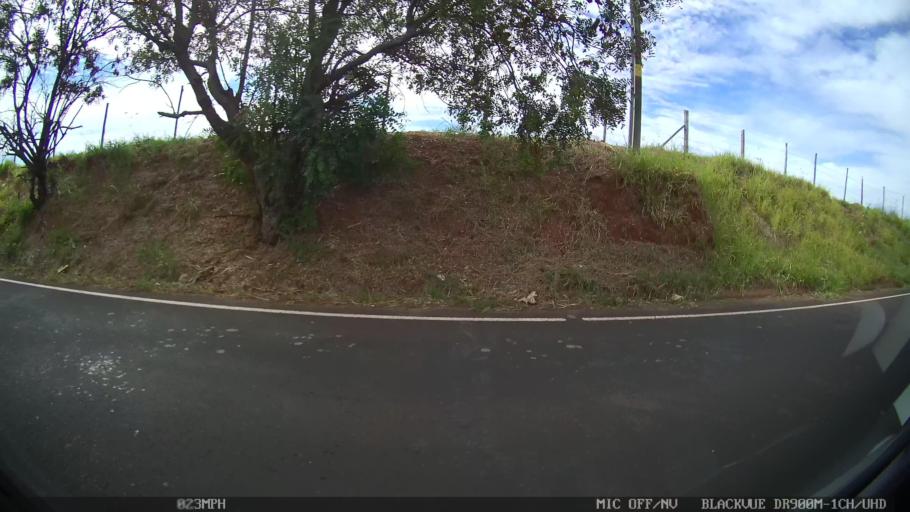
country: BR
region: Sao Paulo
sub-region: Catanduva
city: Catanduva
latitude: -21.1564
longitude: -48.9632
